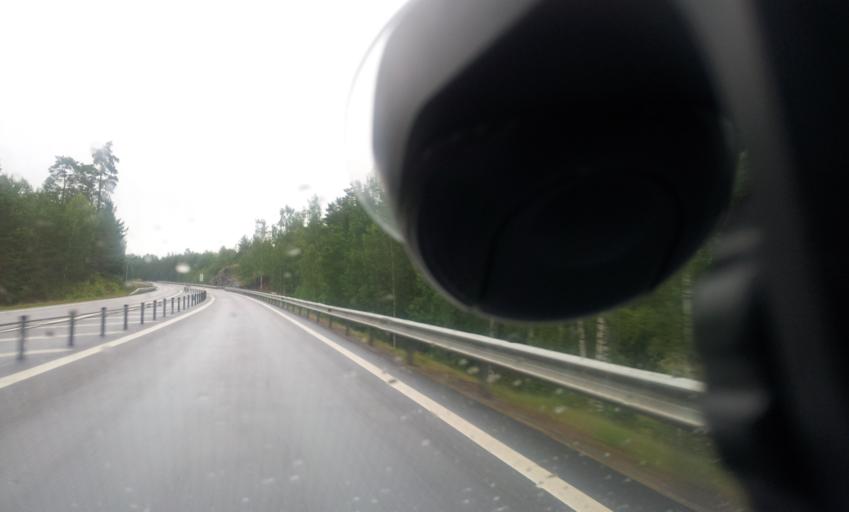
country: SE
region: OEstergoetland
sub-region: Valdemarsviks Kommun
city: Valdemarsvik
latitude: 58.0982
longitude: 16.5346
